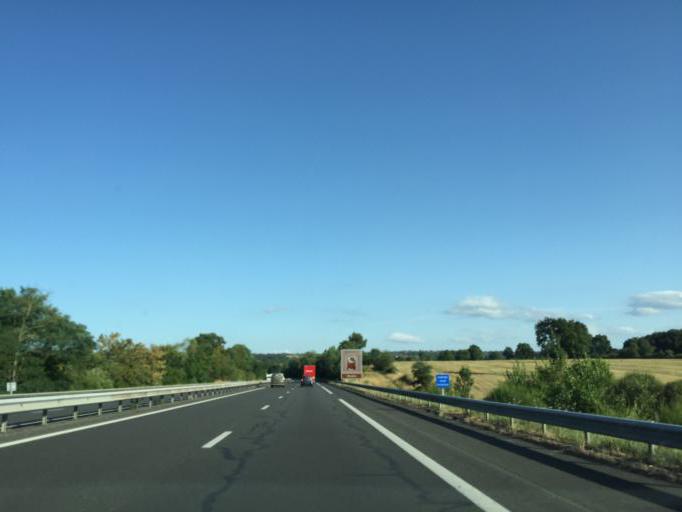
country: FR
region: Auvergne
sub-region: Departement de l'Allier
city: Montmarault
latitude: 46.3363
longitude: 2.8866
